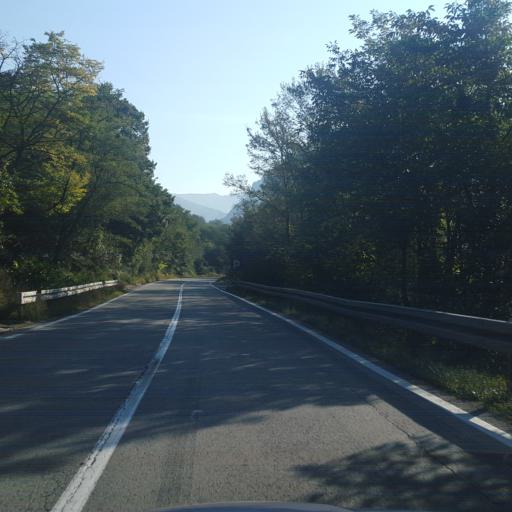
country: RS
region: Central Serbia
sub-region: Nisavski Okrug
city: Svrljig
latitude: 43.3276
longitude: 22.1036
